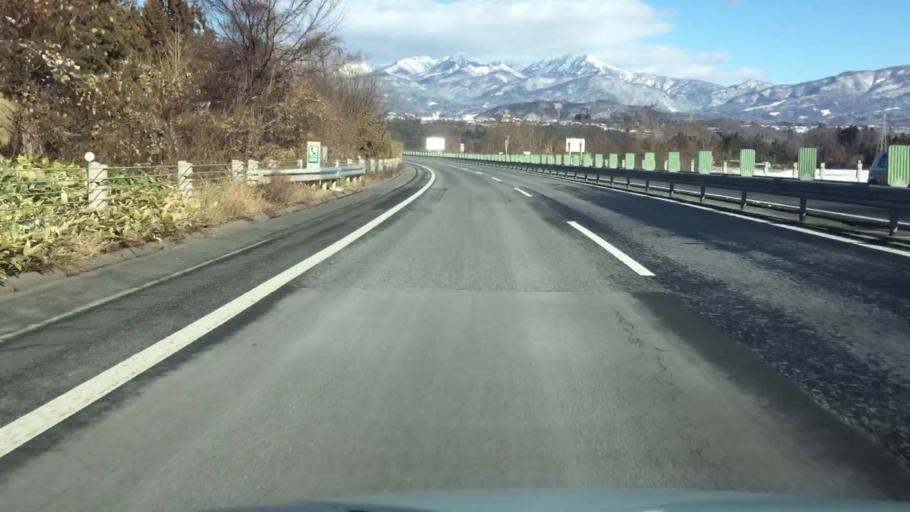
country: JP
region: Gunma
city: Numata
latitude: 36.6425
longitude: 139.0798
